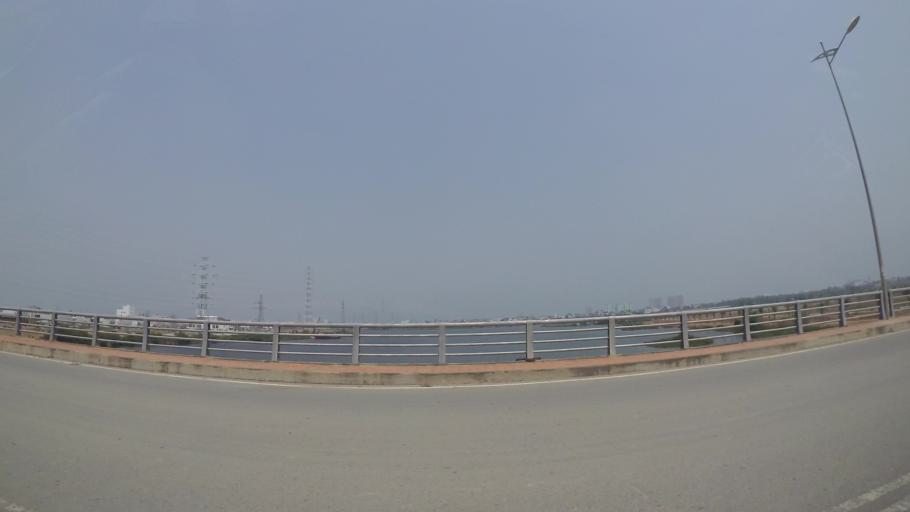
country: VN
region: Da Nang
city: Ngu Hanh Son
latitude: 16.0148
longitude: 108.2356
